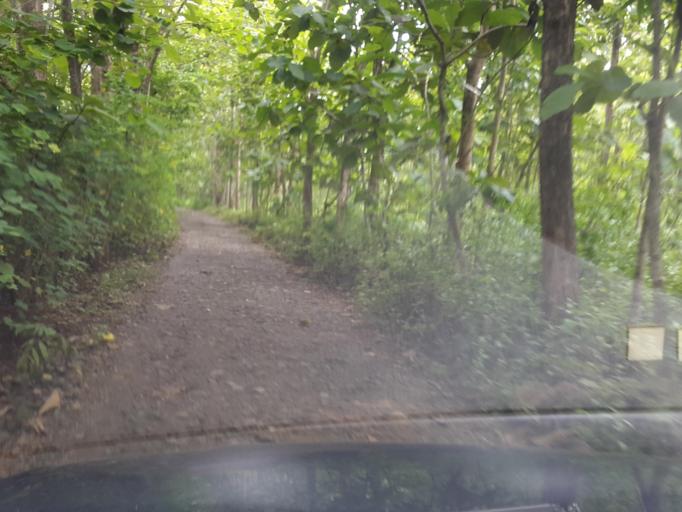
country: ID
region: Daerah Istimewa Yogyakarta
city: Wonosari
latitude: -7.9222
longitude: 110.6389
